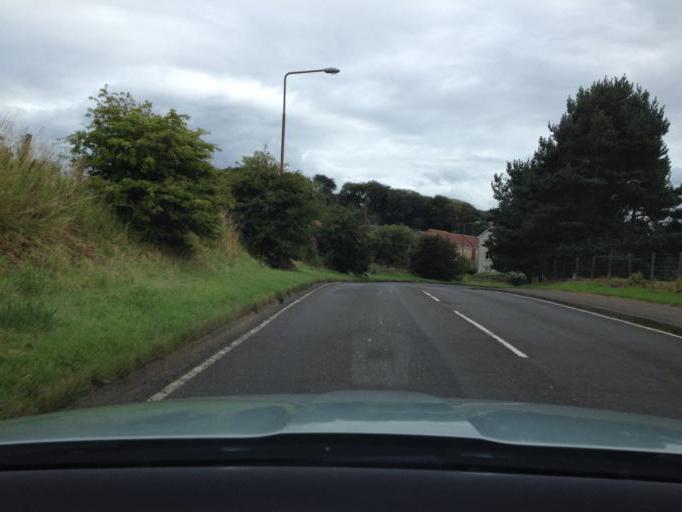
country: GB
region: Scotland
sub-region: West Lothian
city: Bathgate
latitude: 55.9115
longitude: -3.6386
